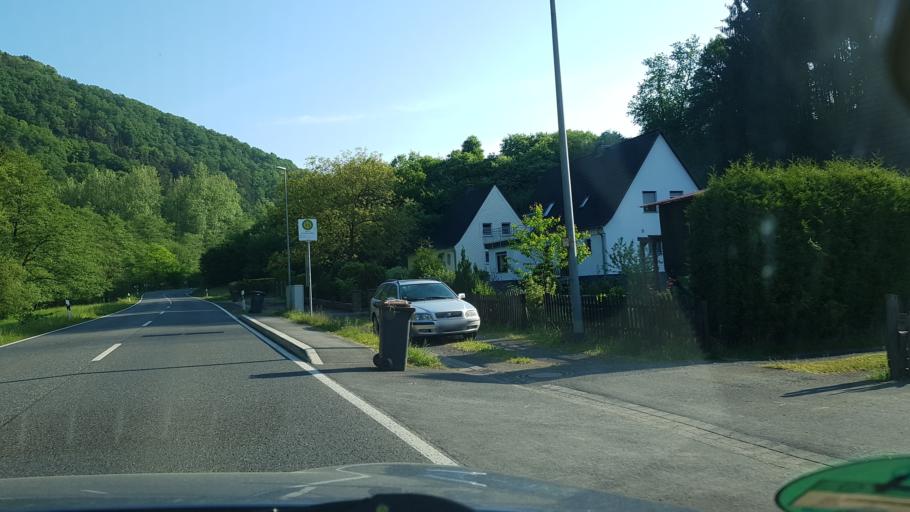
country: DE
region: Rheinland-Pfalz
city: Eitelborn
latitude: 50.3589
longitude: 7.7256
